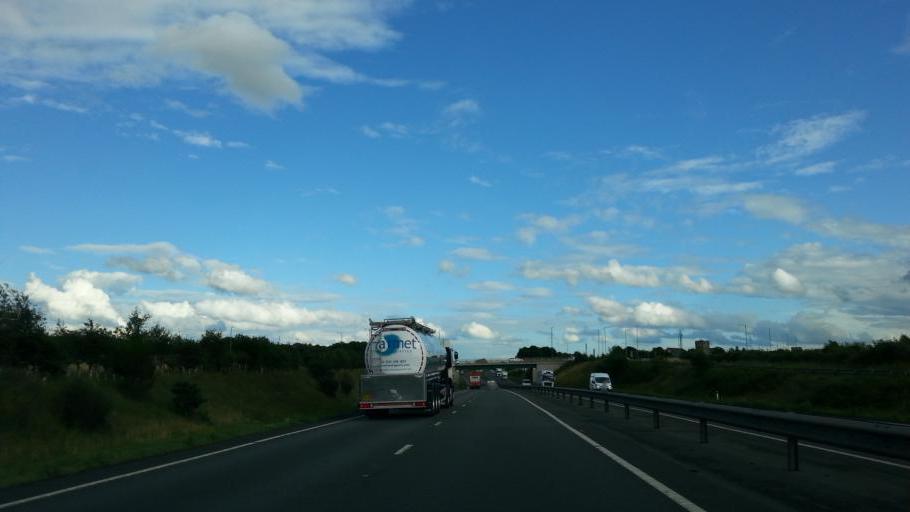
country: GB
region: England
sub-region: Nottinghamshire
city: Bircotes
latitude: 53.3897
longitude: -1.0668
